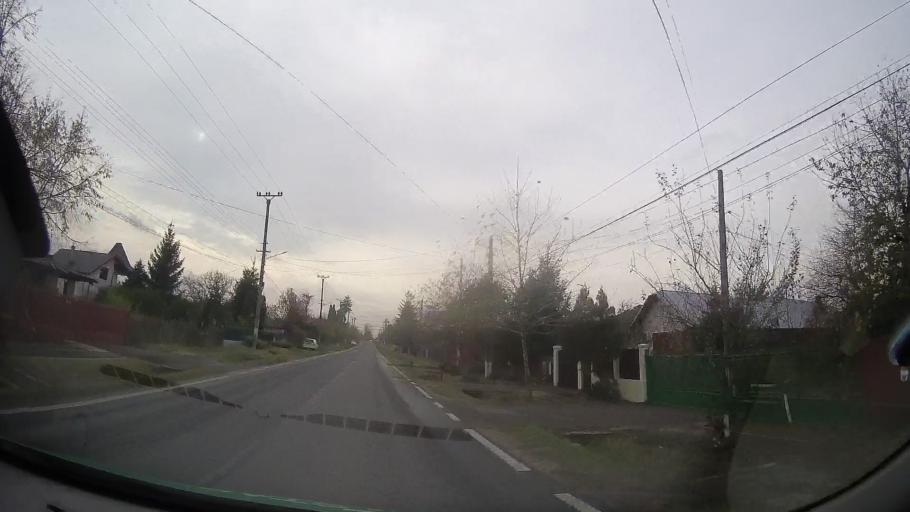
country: RO
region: Ilfov
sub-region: Comuna Gruiu
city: Silistea Snagovului
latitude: 44.7488
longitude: 26.1884
